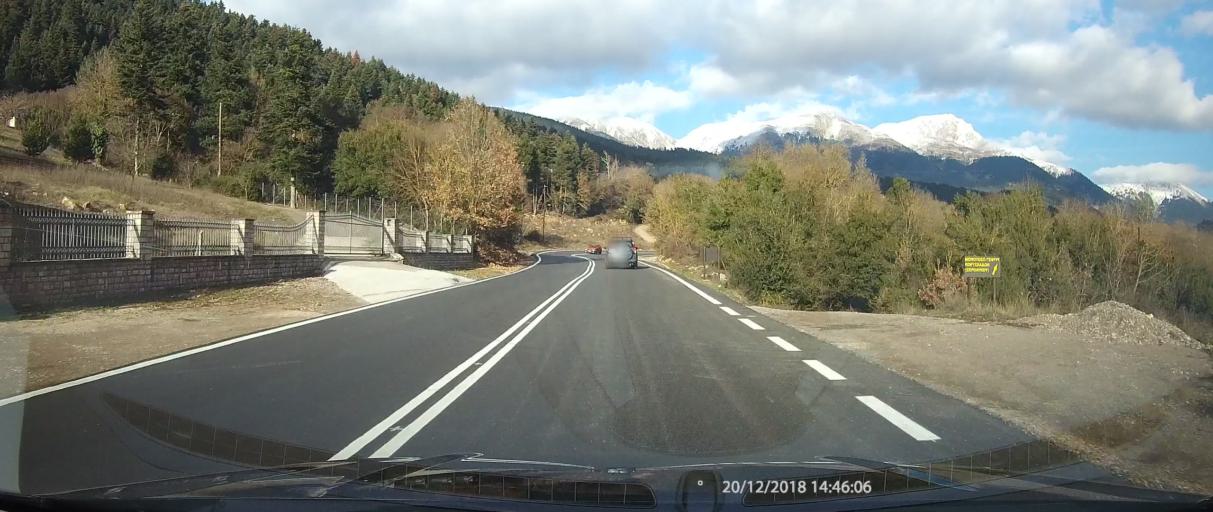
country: GR
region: Central Greece
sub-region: Nomos Evrytanias
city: Karpenisi
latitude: 38.8942
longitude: 21.7648
